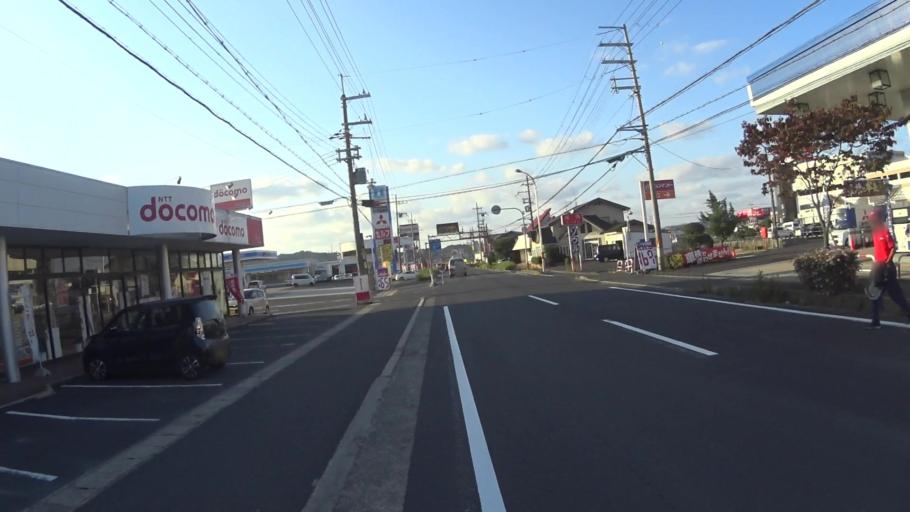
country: JP
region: Kyoto
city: Miyazu
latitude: 35.6066
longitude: 135.0818
